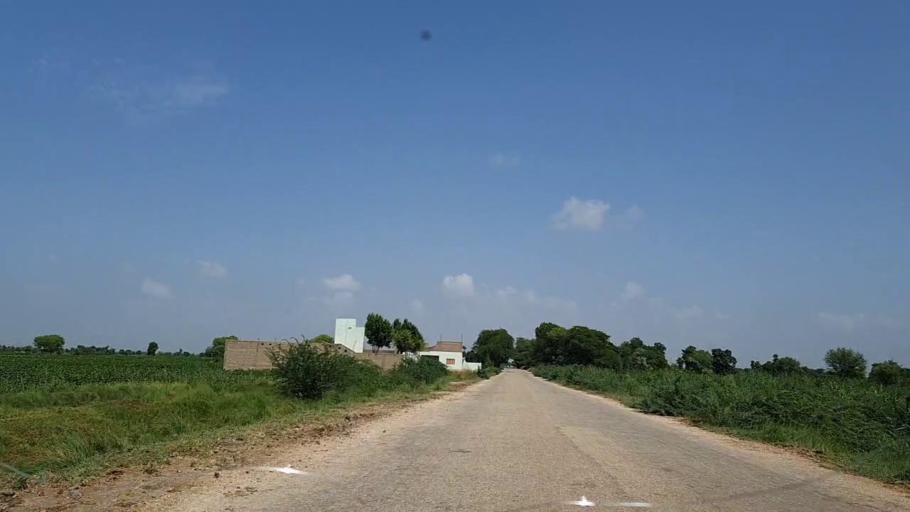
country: PK
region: Sindh
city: Pad Idan
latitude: 26.7937
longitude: 68.2456
